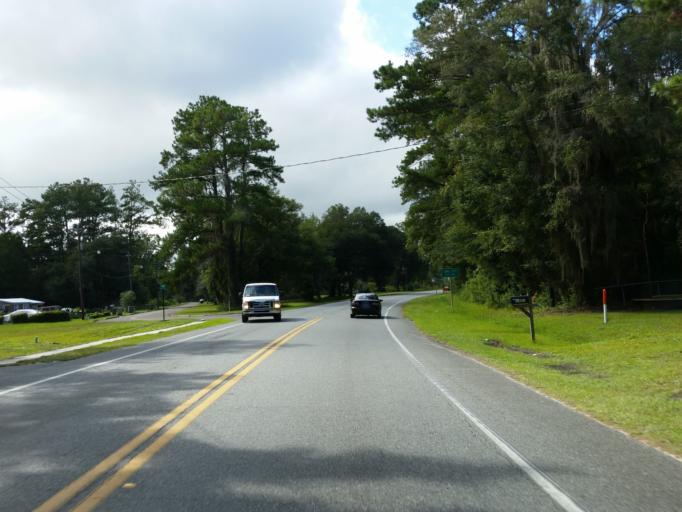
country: US
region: Florida
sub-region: Columbia County
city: Watertown
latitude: 30.1967
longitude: -82.6196
